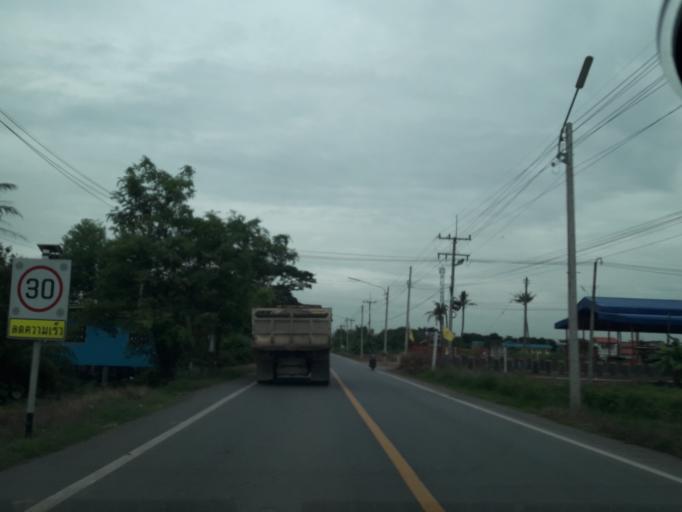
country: TH
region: Pathum Thani
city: Ban Lam Luk Ka
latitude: 14.0138
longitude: 100.8231
